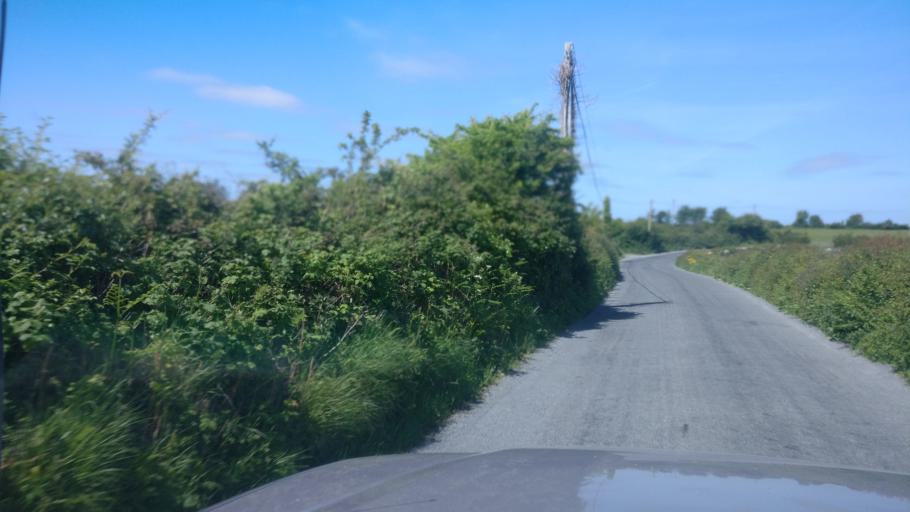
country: IE
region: Connaught
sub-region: County Galway
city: Gort
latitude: 53.0766
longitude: -8.8011
